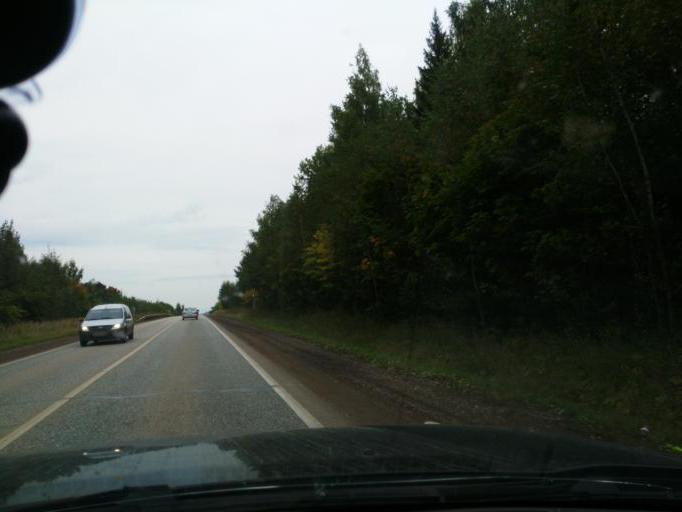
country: RU
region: Perm
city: Chernushka
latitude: 56.5843
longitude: 56.1453
